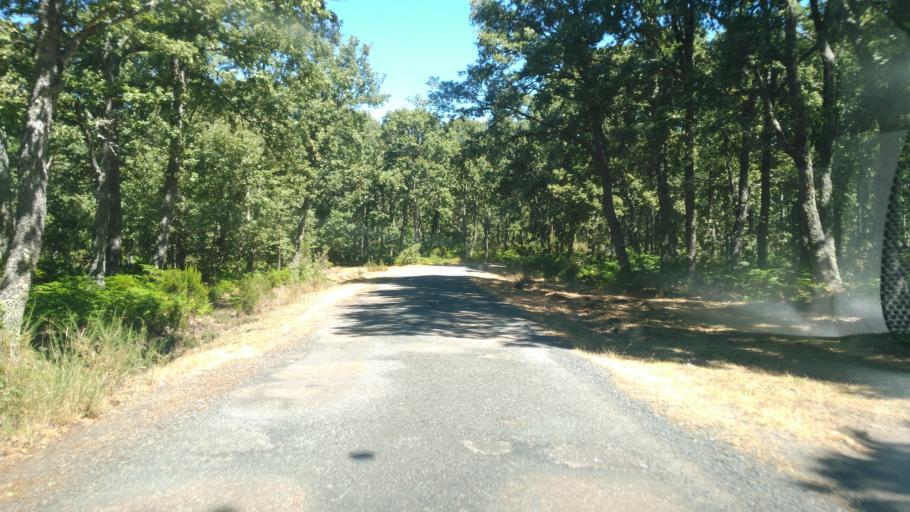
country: ES
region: Castille and Leon
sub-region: Provincia de Salamanca
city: Nava de Francia
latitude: 40.5205
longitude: -6.0999
